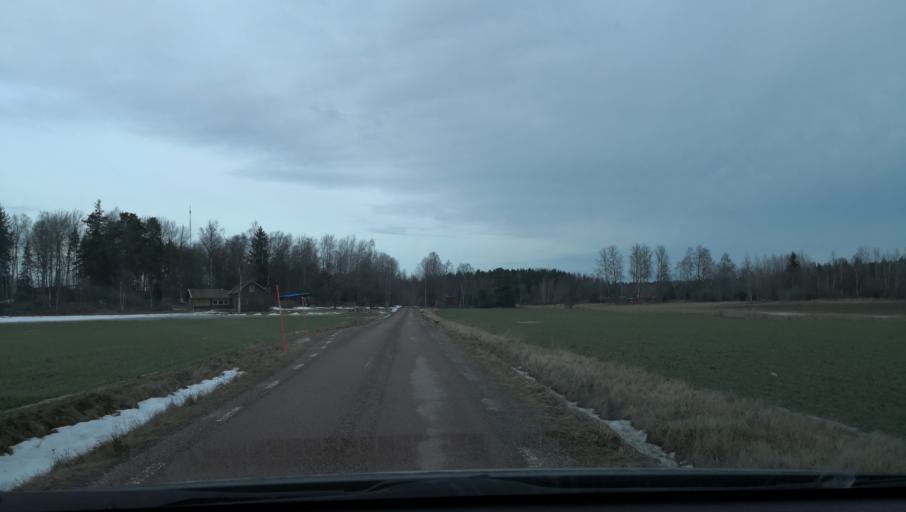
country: SE
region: Vaestmanland
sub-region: Vasteras
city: Skultuna
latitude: 59.6231
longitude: 16.4131
